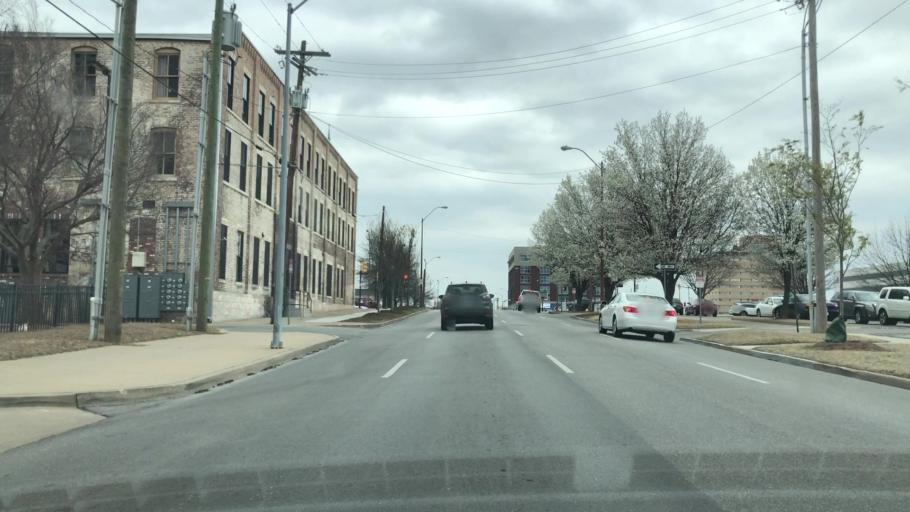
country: US
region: Oklahoma
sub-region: Tulsa County
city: Tulsa
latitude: 36.1483
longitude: -95.9895
